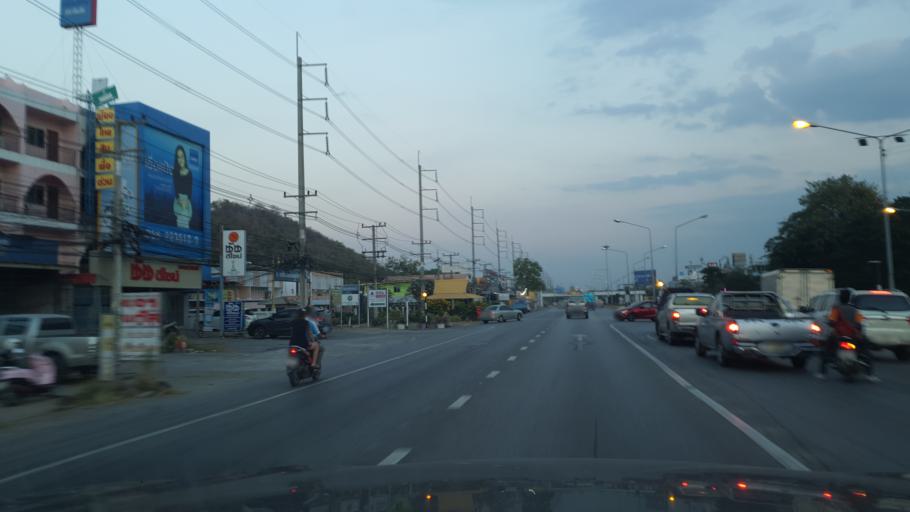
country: TH
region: Nakhon Sawan
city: Nakhon Sawan
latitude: 15.7070
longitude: 100.1051
